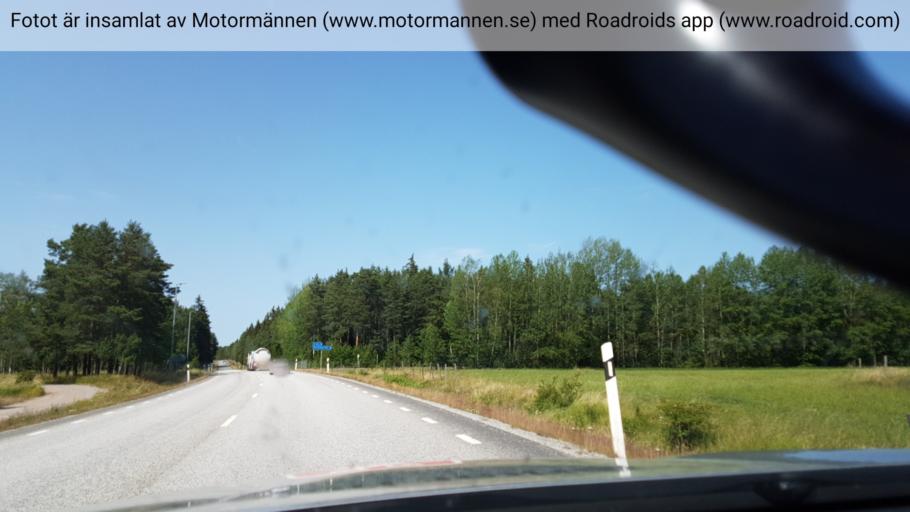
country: SE
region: Joenkoeping
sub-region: Eksjo Kommun
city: Eksjoe
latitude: 57.6894
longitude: 14.9554
